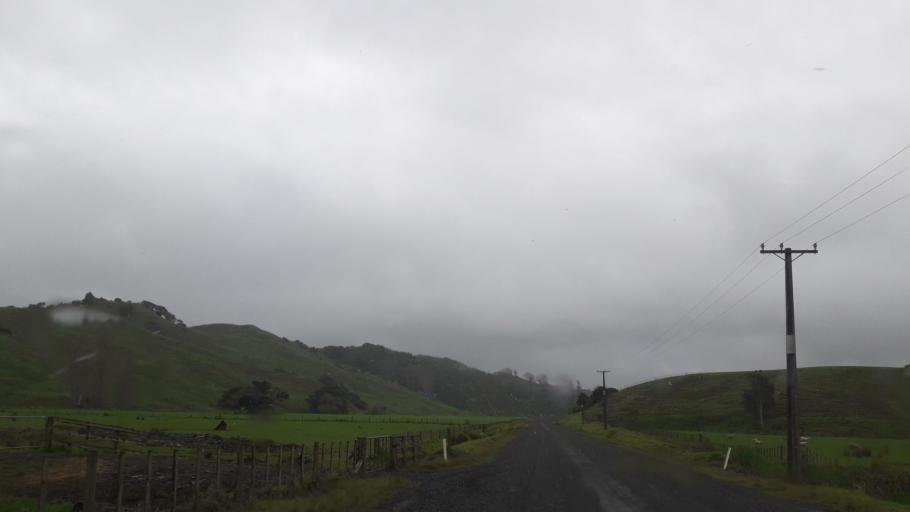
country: NZ
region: Northland
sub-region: Far North District
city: Ahipara
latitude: -35.4211
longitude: 173.3607
